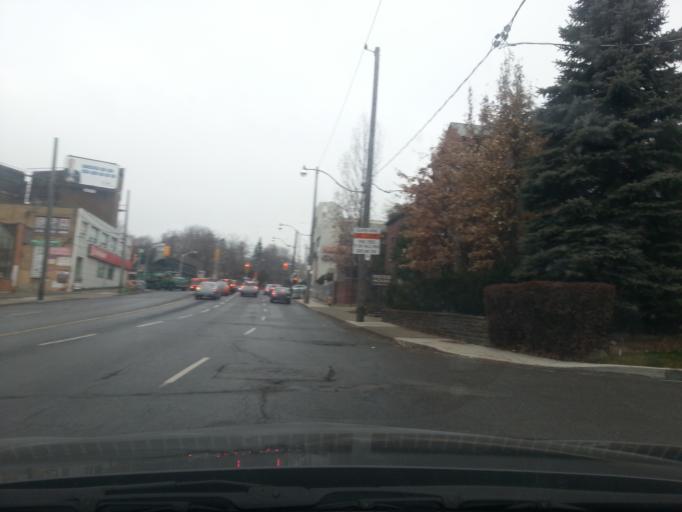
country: CA
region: Ontario
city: Toronto
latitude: 43.7002
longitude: -79.4251
